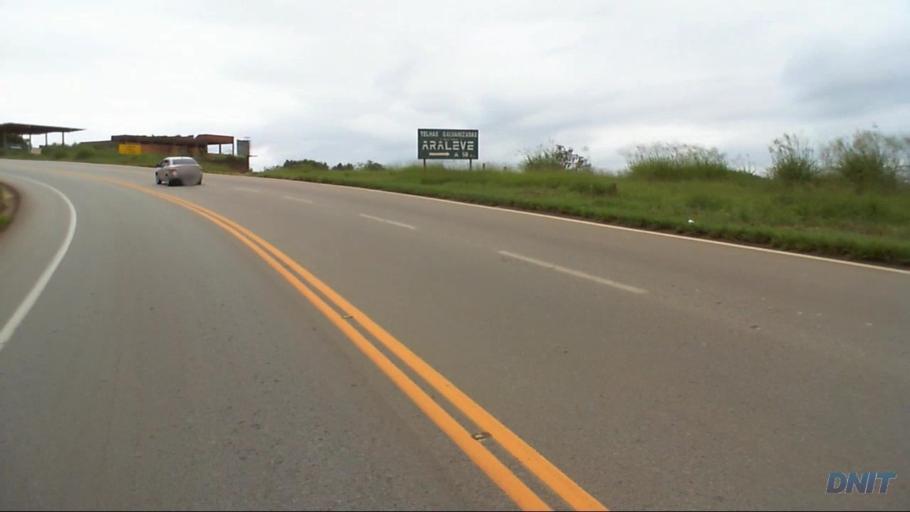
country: BR
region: Minas Gerais
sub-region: Nova Era
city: Nova Era
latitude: -19.8117
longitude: -43.0627
